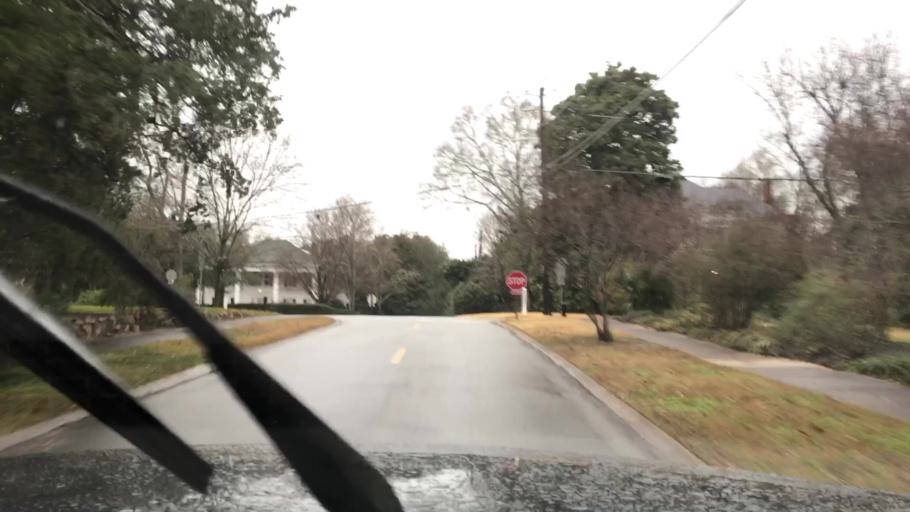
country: US
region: Georgia
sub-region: Morgan County
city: Madison
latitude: 33.5901
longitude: -83.4746
